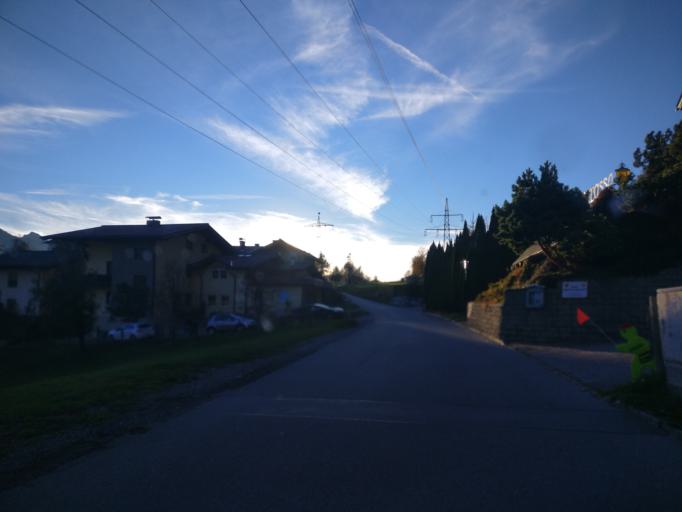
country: AT
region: Salzburg
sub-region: Politischer Bezirk Sankt Johann im Pongau
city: Sankt Veit im Pongau
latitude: 47.3339
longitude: 13.1479
